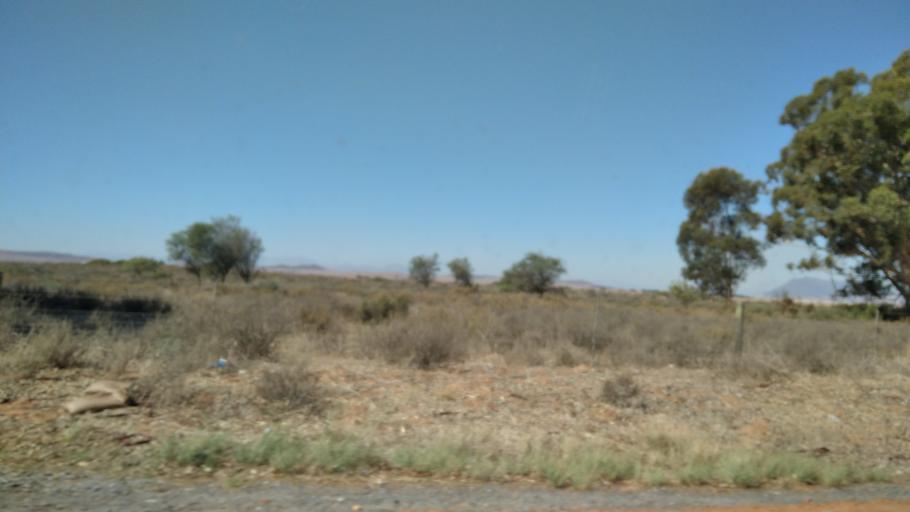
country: ZA
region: Western Cape
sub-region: West Coast District Municipality
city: Moorreesburg
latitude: -33.2708
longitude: 18.5997
